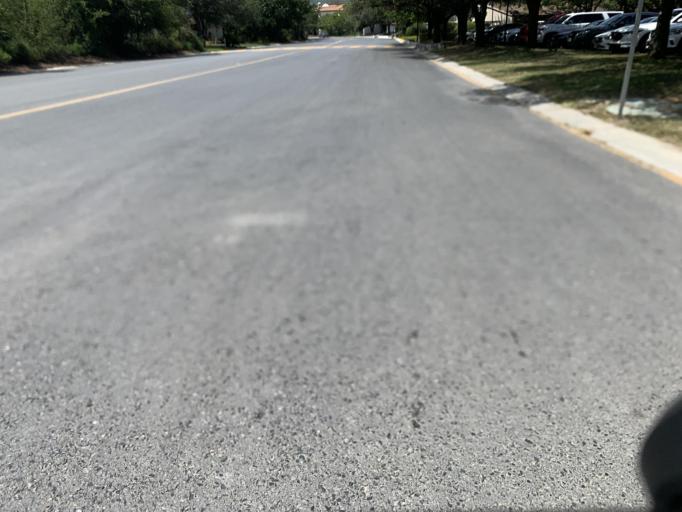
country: MX
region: Nuevo Leon
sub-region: Juarez
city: Bosques de San Pedro
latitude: 25.5154
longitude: -100.1911
